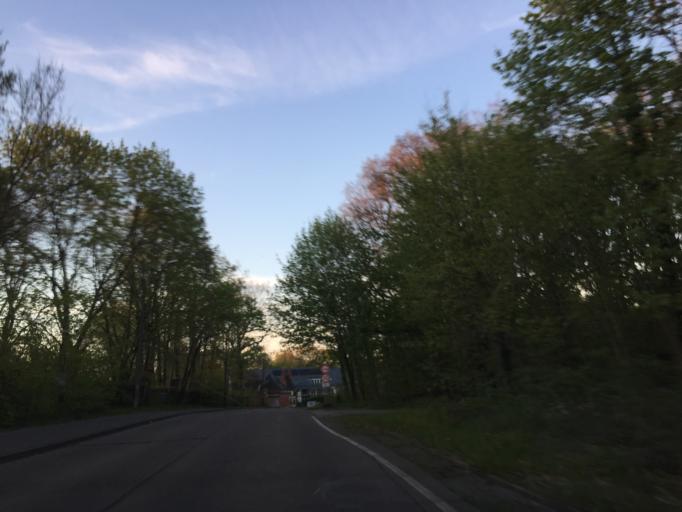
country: DE
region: Brandenburg
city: Potsdam
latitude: 52.3819
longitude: 13.0434
